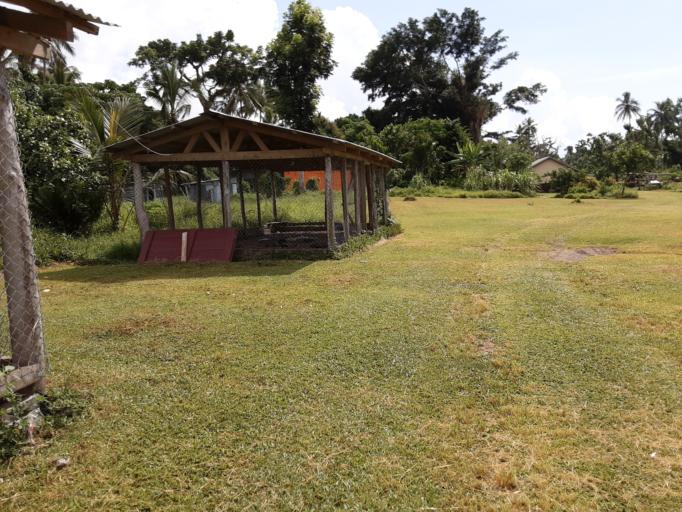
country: VU
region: Sanma
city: Luganville
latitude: -15.5799
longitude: 167.0007
